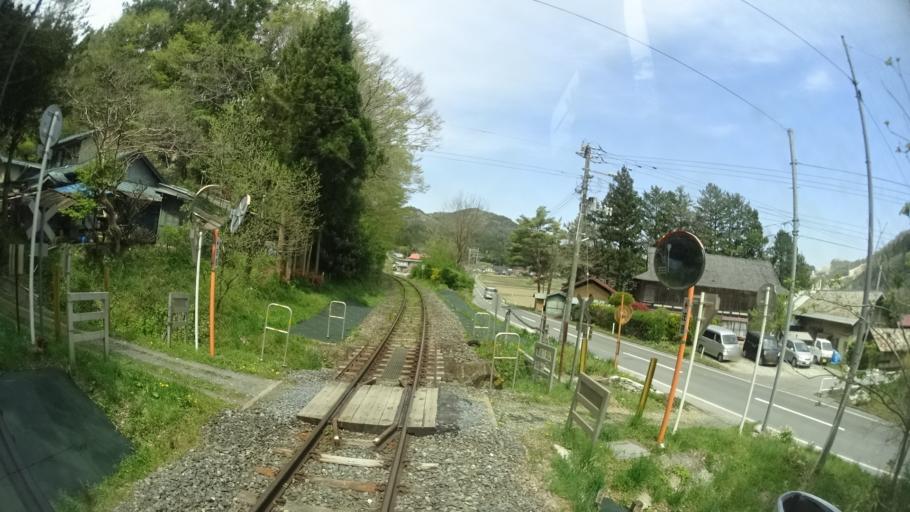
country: JP
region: Iwate
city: Ichinoseki
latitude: 38.9602
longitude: 141.2435
